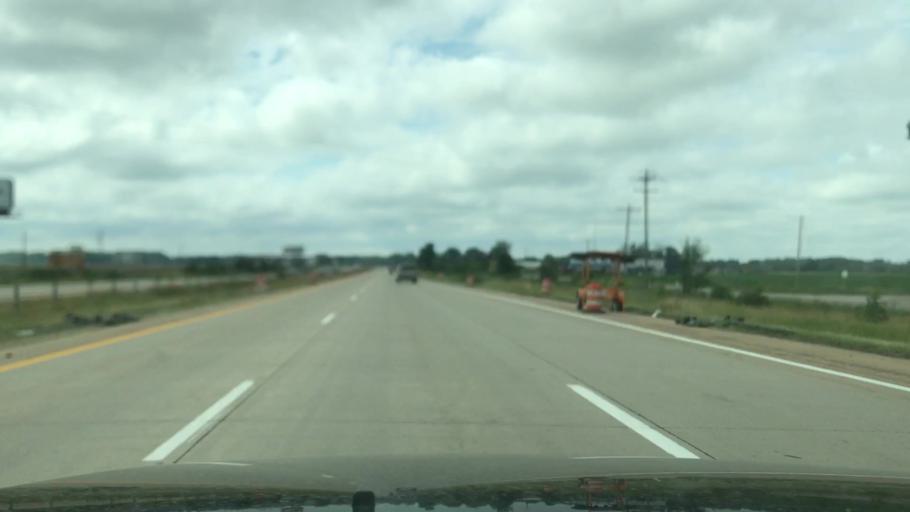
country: US
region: Michigan
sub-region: Ottawa County
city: Coopersville
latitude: 43.0616
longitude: -85.9664
